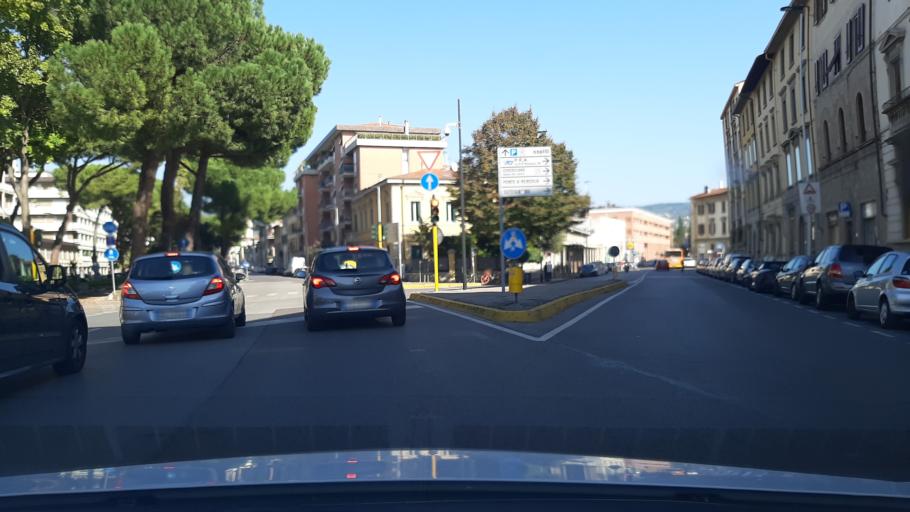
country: IT
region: Tuscany
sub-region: Province of Florence
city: Fiesole
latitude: 43.7744
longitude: 11.2870
